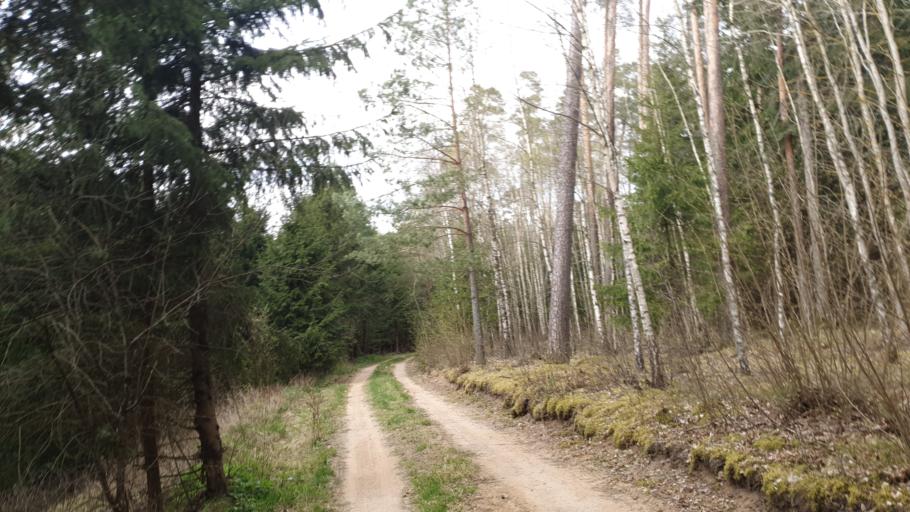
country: LT
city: Aukstadvaris
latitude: 54.5134
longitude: 24.6412
